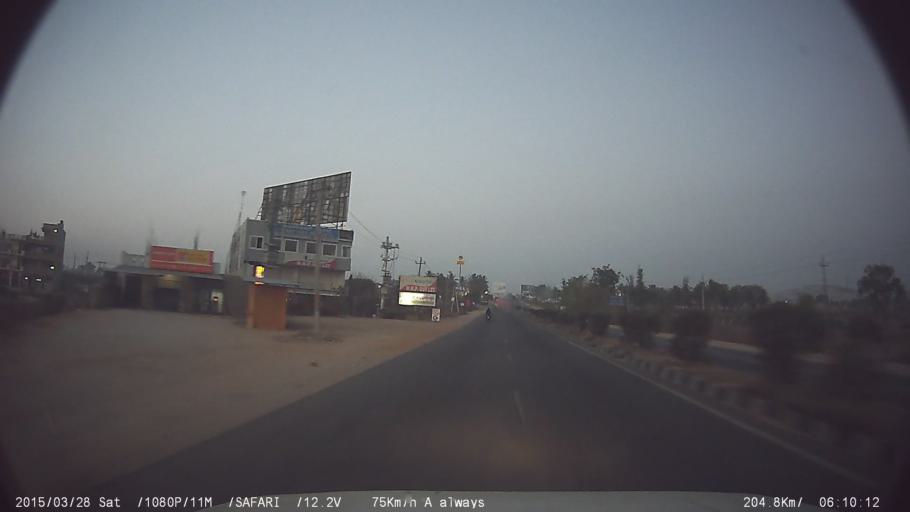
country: IN
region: Karnataka
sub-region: Ramanagara
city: Ramanagaram
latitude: 12.7926
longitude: 77.3799
